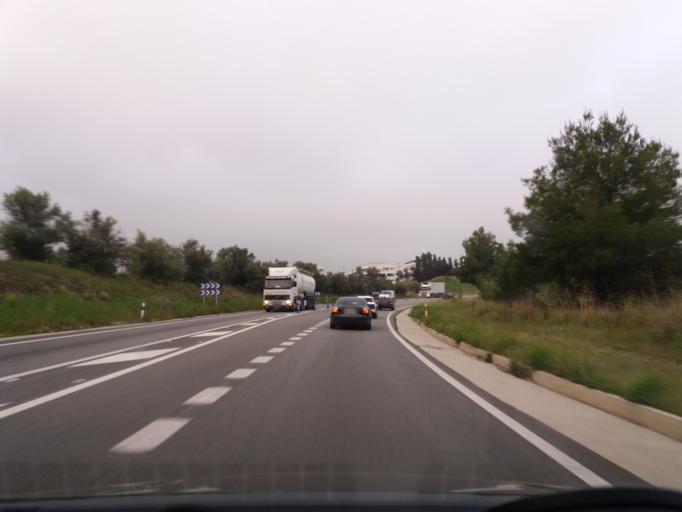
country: ES
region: Catalonia
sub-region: Provincia de Barcelona
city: Abrera
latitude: 41.5269
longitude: 1.9060
